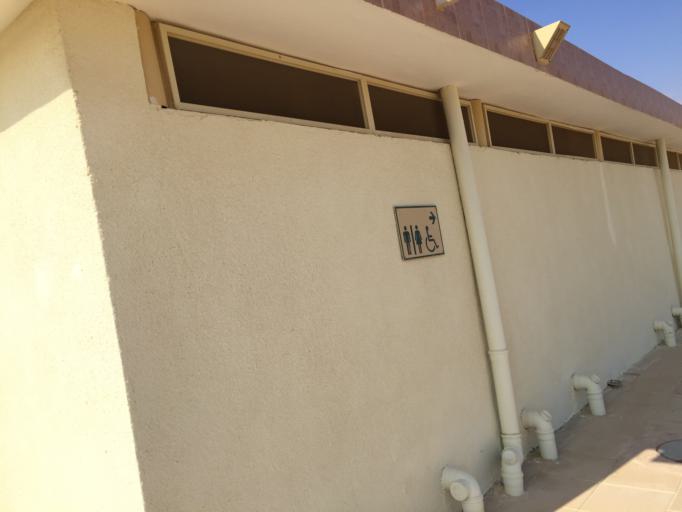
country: IL
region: Southern District
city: `En Boqeq
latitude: 31.3188
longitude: 35.3477
